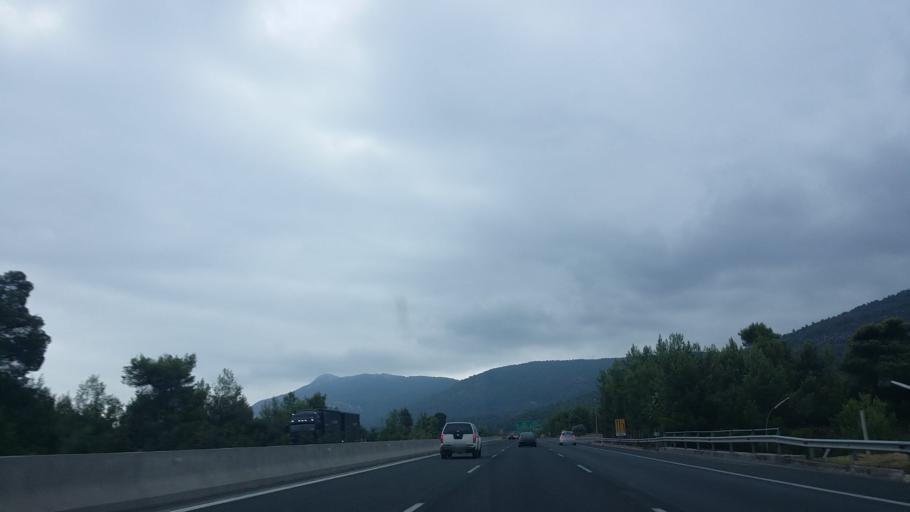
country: GR
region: Attica
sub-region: Nomarchia Anatolikis Attikis
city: Oropos
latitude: 38.2476
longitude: 23.7668
